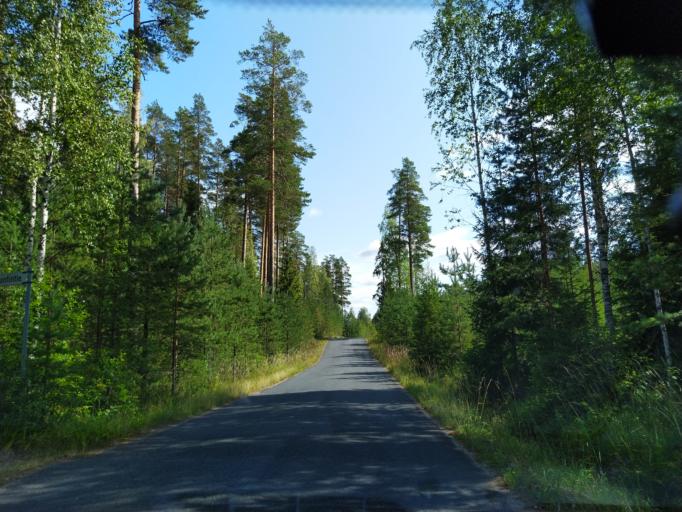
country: FI
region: Uusimaa
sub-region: Helsinki
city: Karkkila
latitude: 60.7181
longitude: 24.2077
